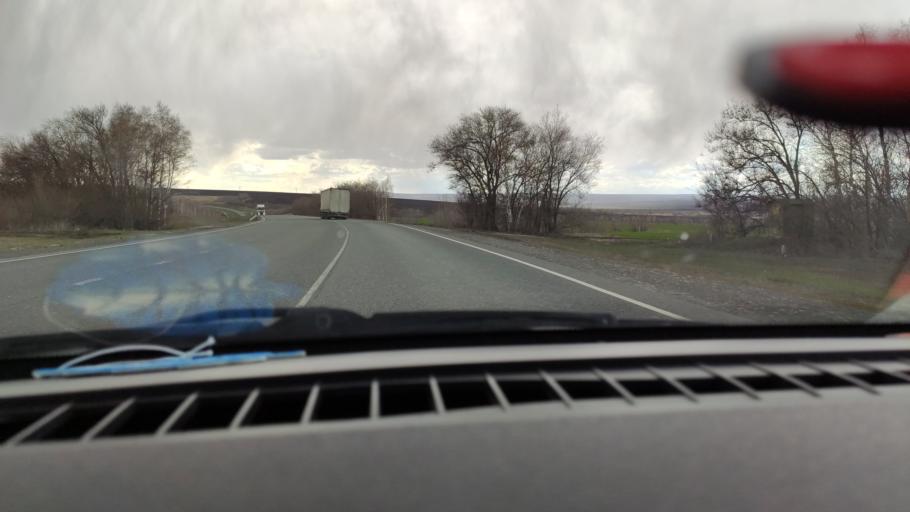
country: RU
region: Saratov
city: Balakovo
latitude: 52.1325
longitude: 47.7708
